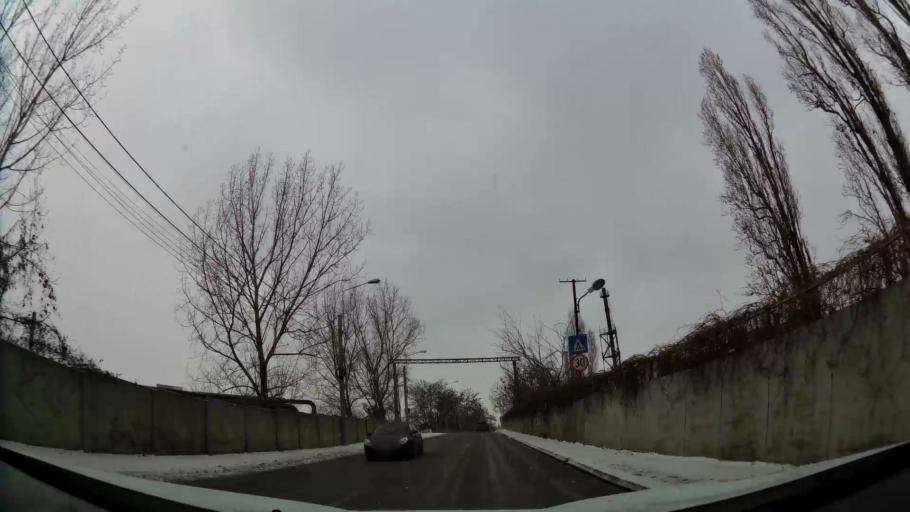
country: RO
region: Prahova
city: Ploiesti
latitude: 44.9230
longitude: 26.0183
